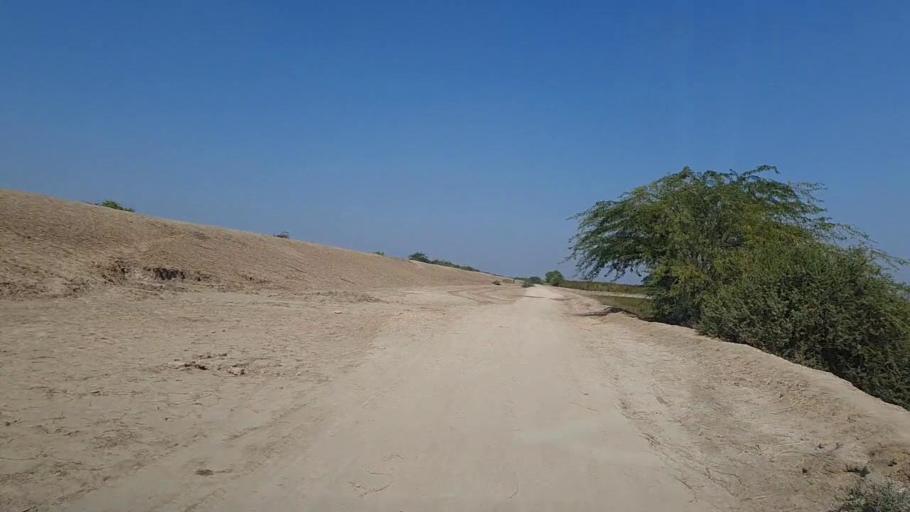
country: PK
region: Sindh
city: Chuhar Jamali
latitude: 24.4801
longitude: 68.0124
